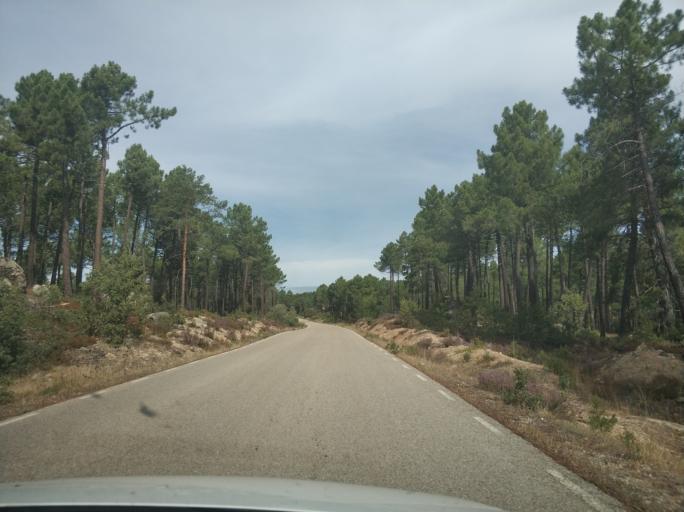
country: ES
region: Castille and Leon
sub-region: Provincia de Soria
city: Duruelo de la Sierra
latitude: 41.8878
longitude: -2.9398
